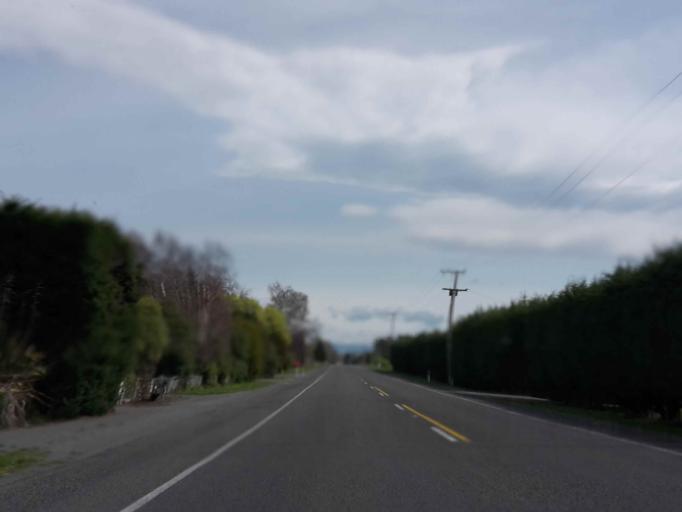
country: NZ
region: Canterbury
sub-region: Waimakariri District
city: Kaiapoi
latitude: -43.4015
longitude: 172.6124
